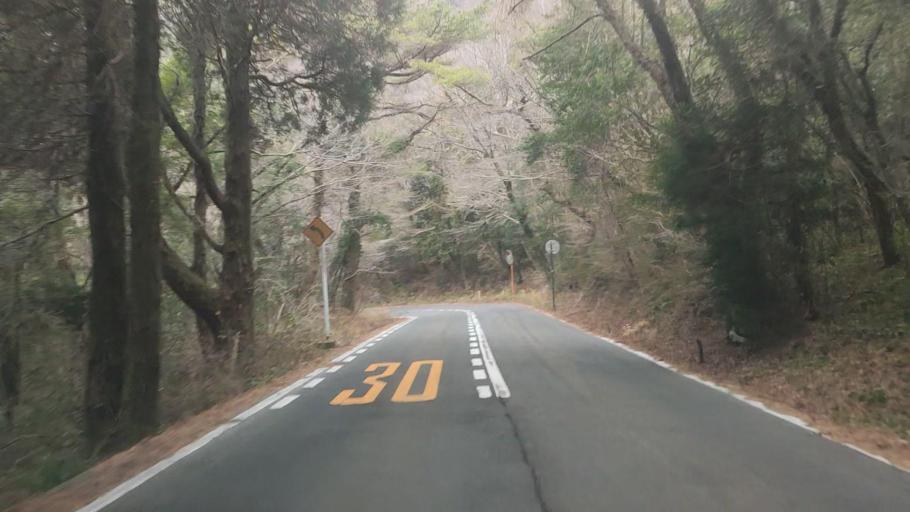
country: JP
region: Nagasaki
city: Shimabara
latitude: 32.7513
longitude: 130.2754
